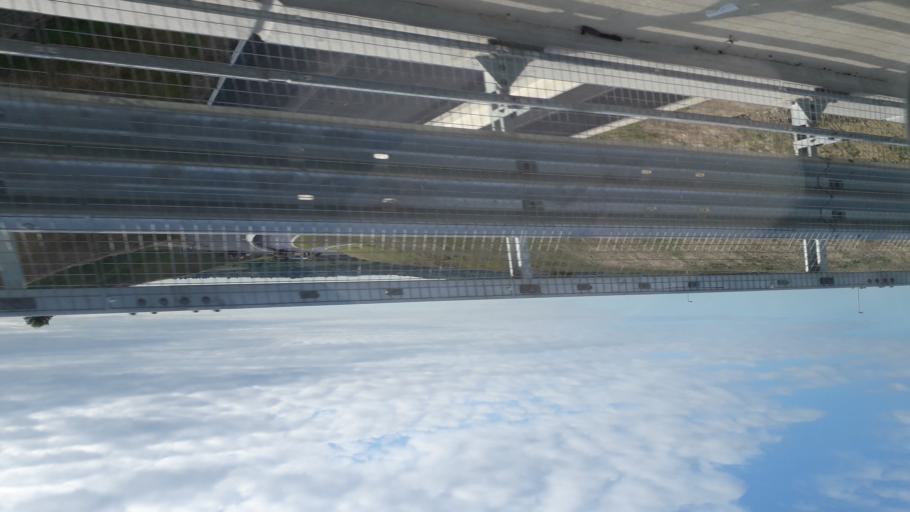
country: IE
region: Leinster
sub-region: Loch Garman
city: Gorey
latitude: 52.6329
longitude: -6.3628
